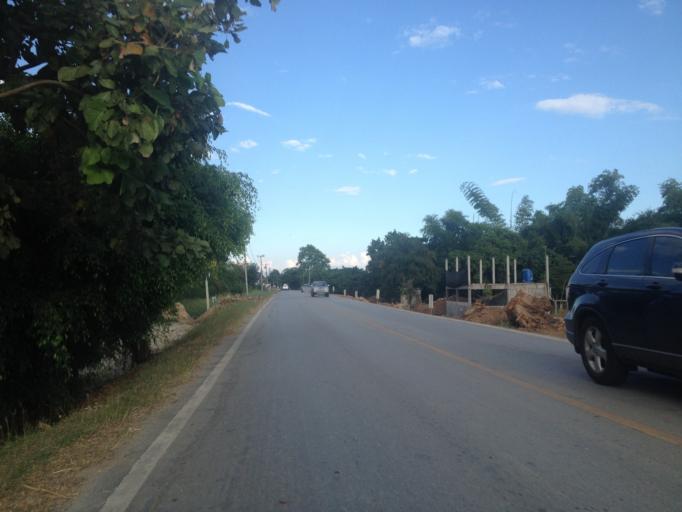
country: TH
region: Chiang Mai
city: San Pa Tong
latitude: 18.6117
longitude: 98.8496
